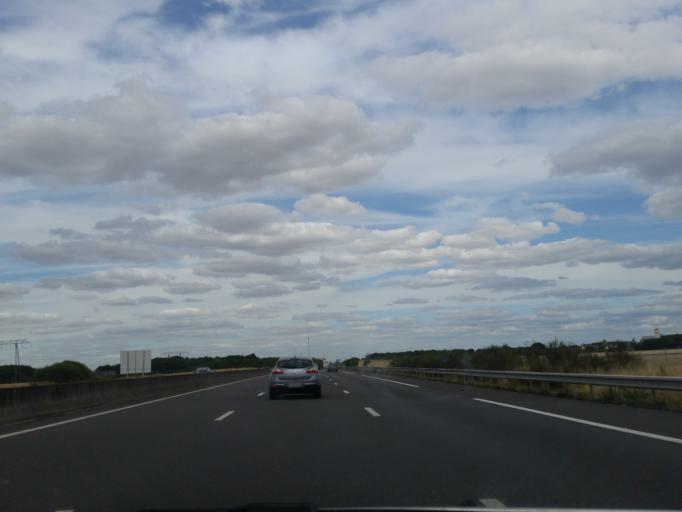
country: FR
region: Centre
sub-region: Departement du Loir-et-Cher
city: Herbault
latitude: 47.6010
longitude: 1.1085
